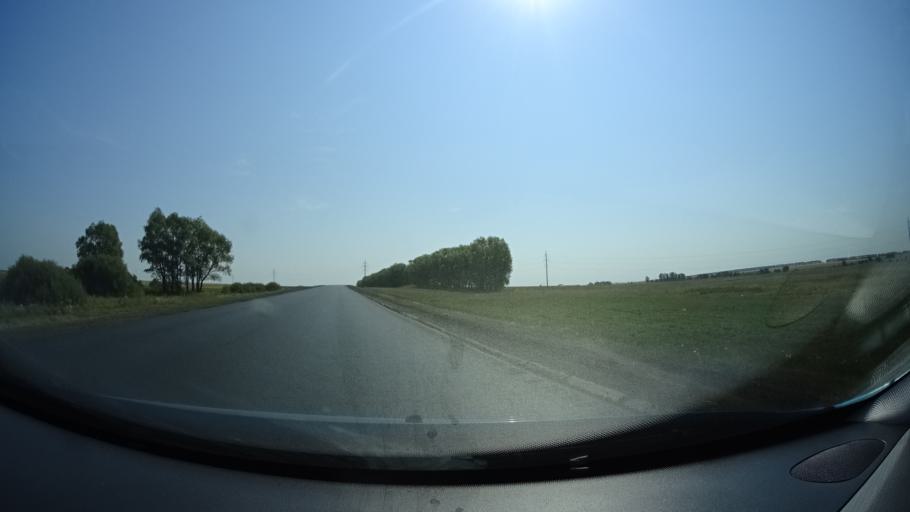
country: RU
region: Bashkortostan
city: Kabakovo
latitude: 54.4361
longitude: 56.0083
